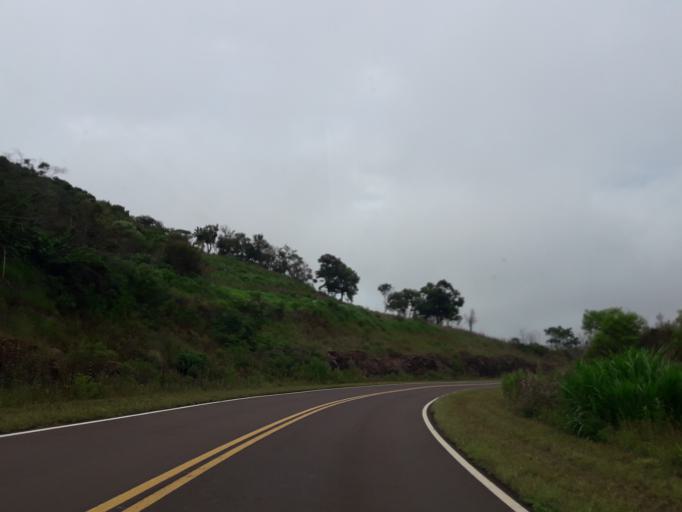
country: AR
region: Misiones
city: Bernardo de Irigoyen
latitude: -26.3957
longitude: -53.8083
